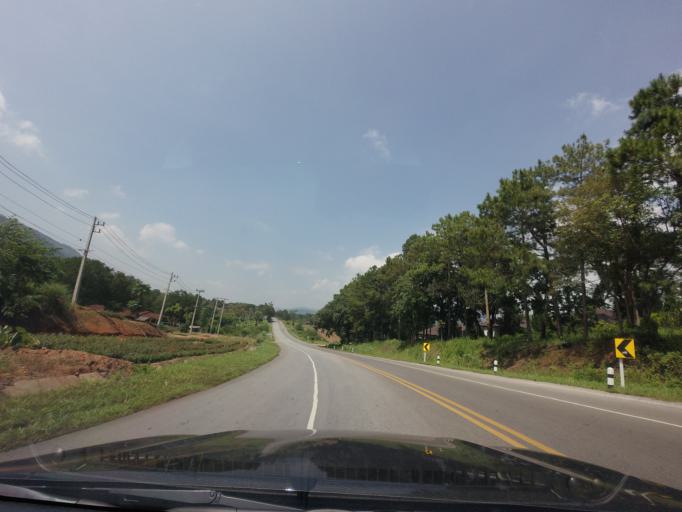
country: TH
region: Loei
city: Phu Ruea
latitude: 17.4593
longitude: 101.4130
